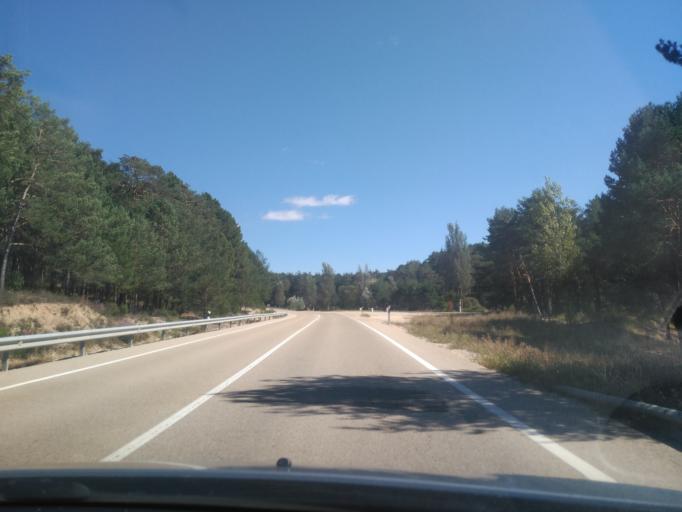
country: ES
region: Castille and Leon
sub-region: Provincia de Soria
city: Navaleno
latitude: 41.8342
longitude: -2.9986
